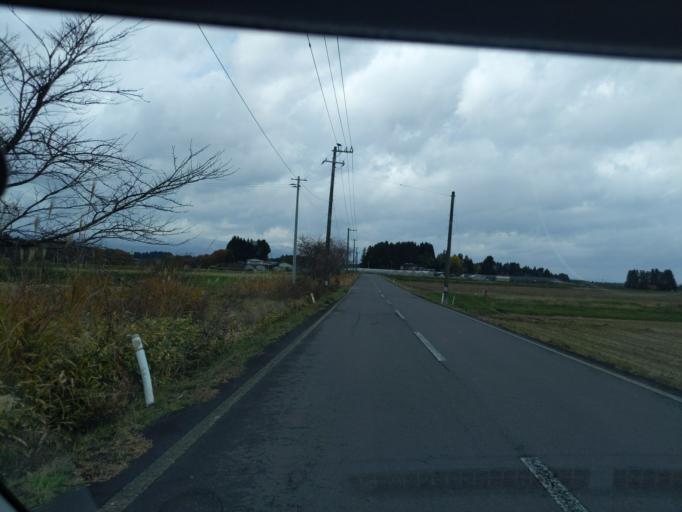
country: JP
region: Iwate
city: Mizusawa
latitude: 39.0675
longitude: 141.0784
